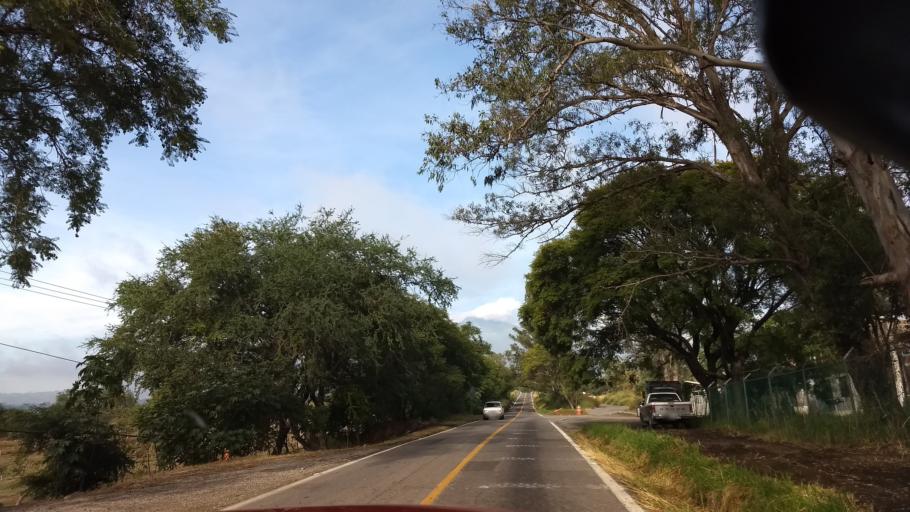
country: MX
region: Jalisco
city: Tuxpan
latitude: 19.5227
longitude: -103.4422
